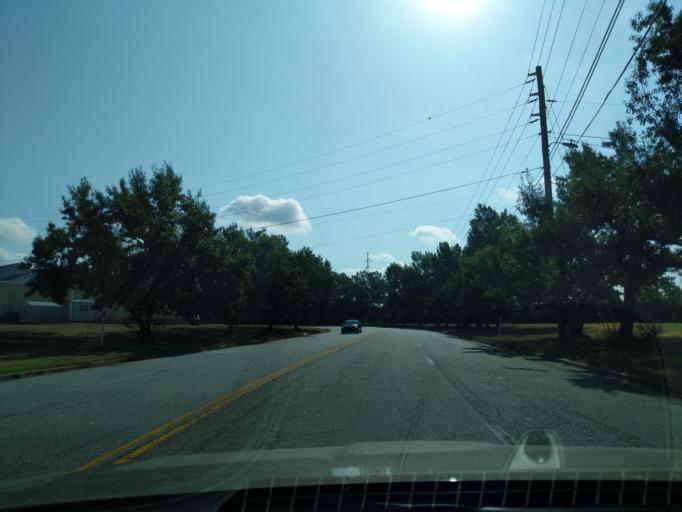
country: US
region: Georgia
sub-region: Richmond County
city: Augusta
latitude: 33.4596
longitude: -81.9744
